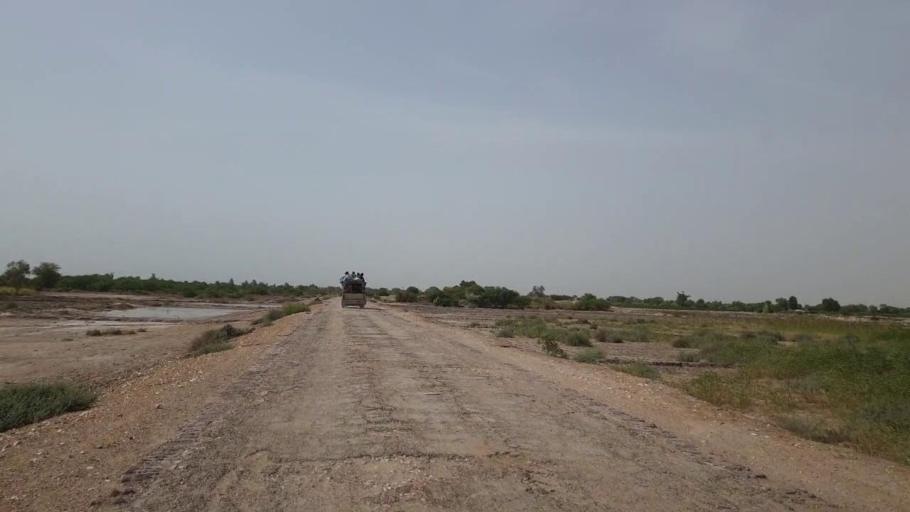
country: PK
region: Sindh
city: Bandhi
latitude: 26.5644
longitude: 68.3810
